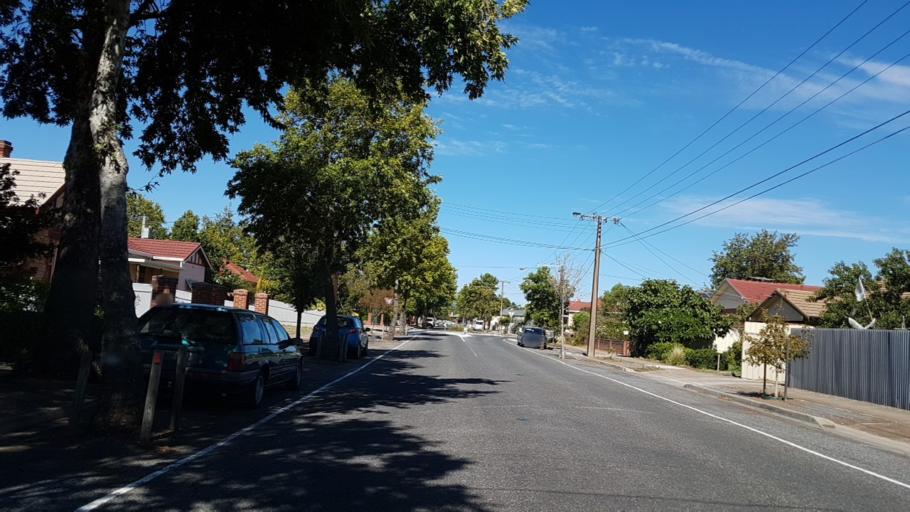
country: AU
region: South Australia
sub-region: City of West Torrens
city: Thebarton
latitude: -34.9201
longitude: 138.5636
